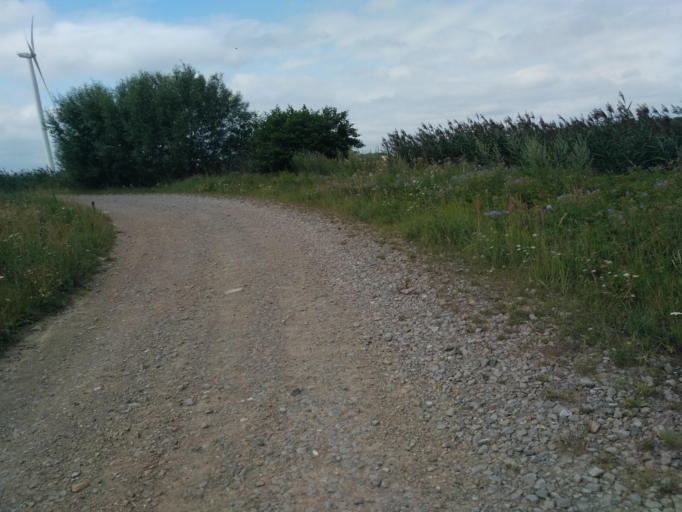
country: PL
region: Subcarpathian Voivodeship
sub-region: Powiat krosnienski
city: Rymanow
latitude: 49.6084
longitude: 21.8430
